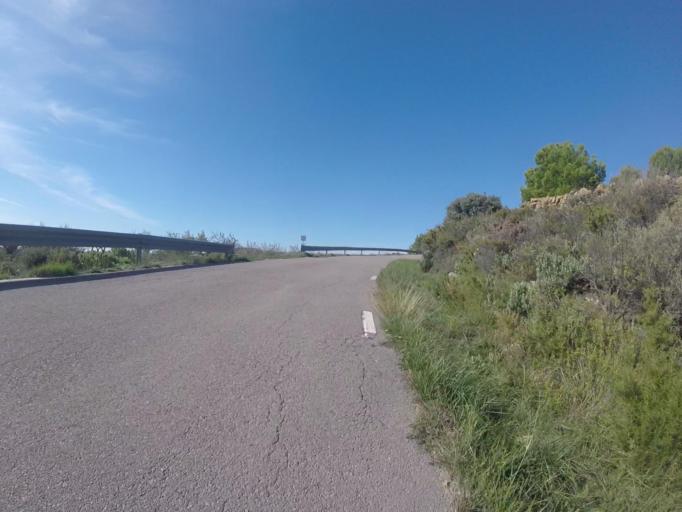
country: ES
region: Valencia
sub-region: Provincia de Castello
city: Sarratella
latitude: 40.2880
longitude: 0.0311
